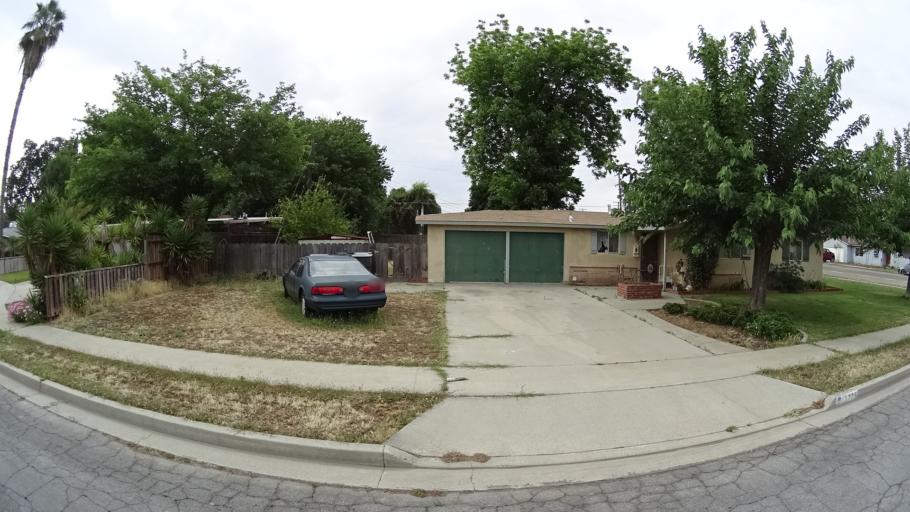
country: US
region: California
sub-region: Kings County
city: Hanford
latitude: 36.3388
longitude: -119.6579
